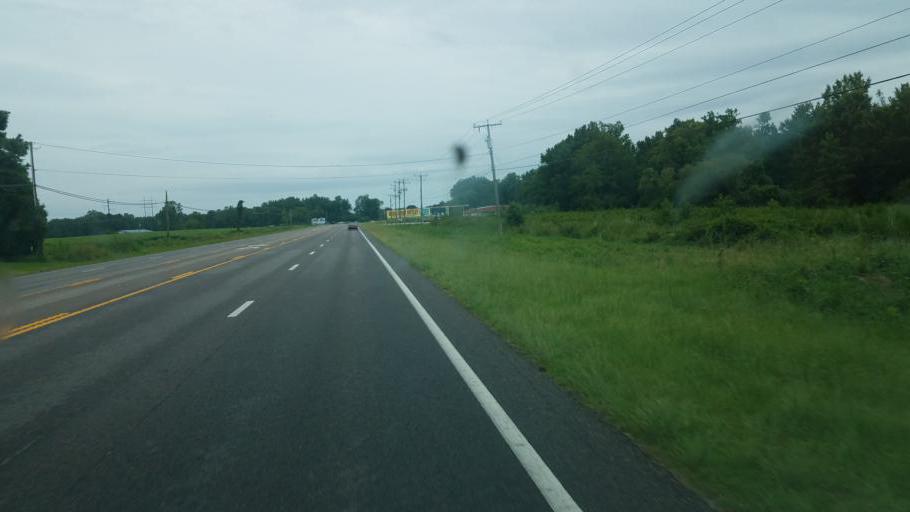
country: US
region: North Carolina
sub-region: Currituck County
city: Currituck
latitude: 36.3303
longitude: -75.9448
